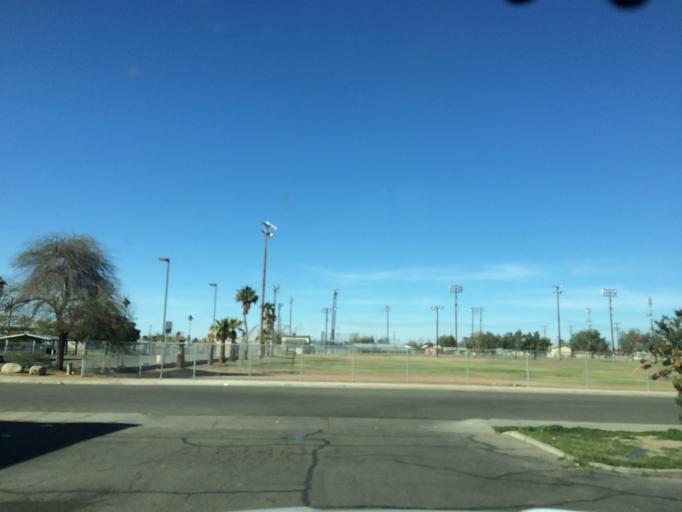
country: US
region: California
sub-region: Imperial County
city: El Centro
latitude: 32.7826
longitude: -115.5516
